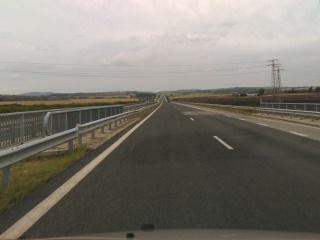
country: BG
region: Stara Zagora
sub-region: Obshtina Chirpan
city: Chirpan
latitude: 42.2079
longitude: 25.3031
